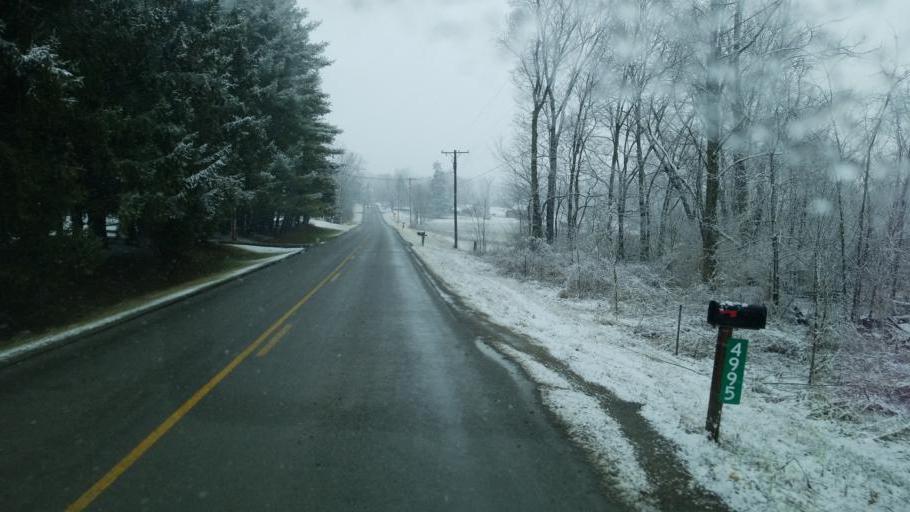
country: US
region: Ohio
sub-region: Logan County
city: Bellefontaine
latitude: 40.3321
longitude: -83.6702
